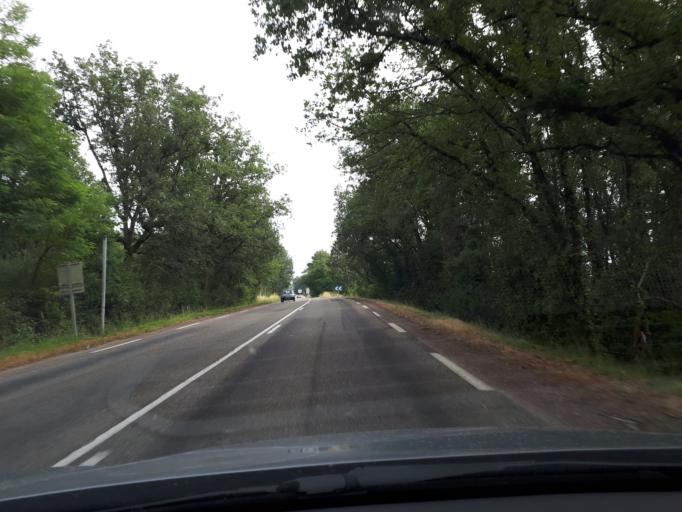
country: FR
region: Midi-Pyrenees
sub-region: Departement du Tarn-et-Garonne
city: Campsas
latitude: 43.9060
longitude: 1.3109
